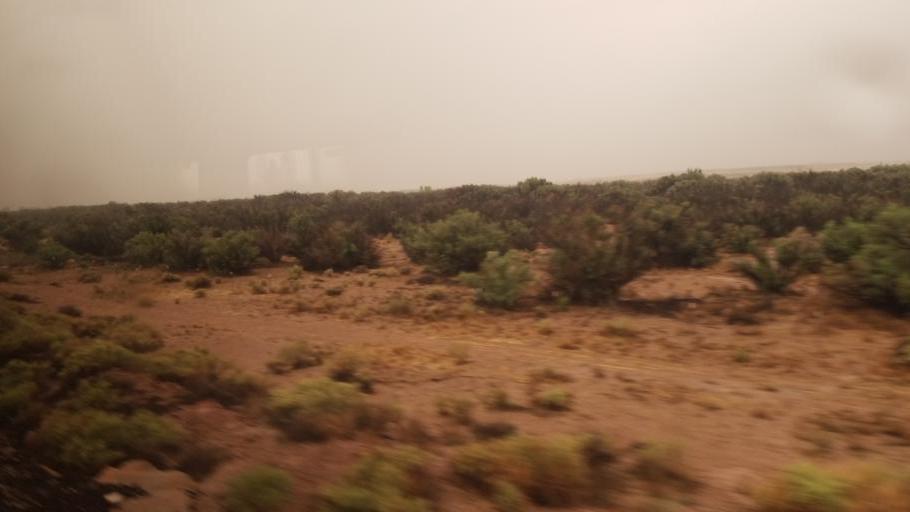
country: US
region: Arizona
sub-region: Navajo County
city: Joseph City
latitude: 34.9556
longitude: -110.3619
